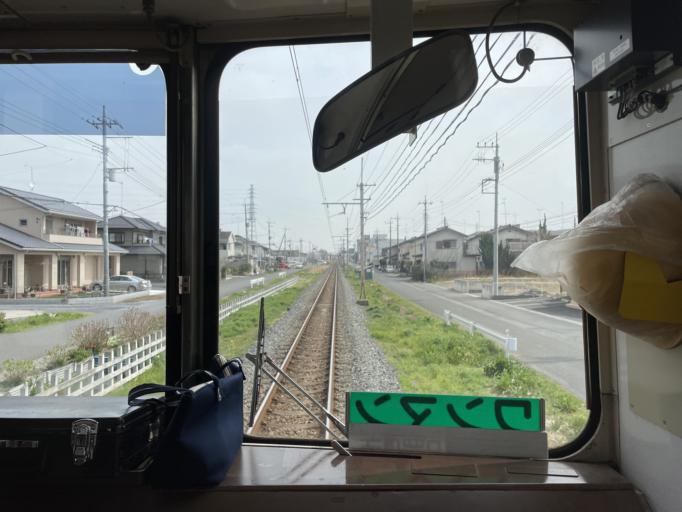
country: JP
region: Saitama
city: Gyoda
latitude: 36.1366
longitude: 139.4266
